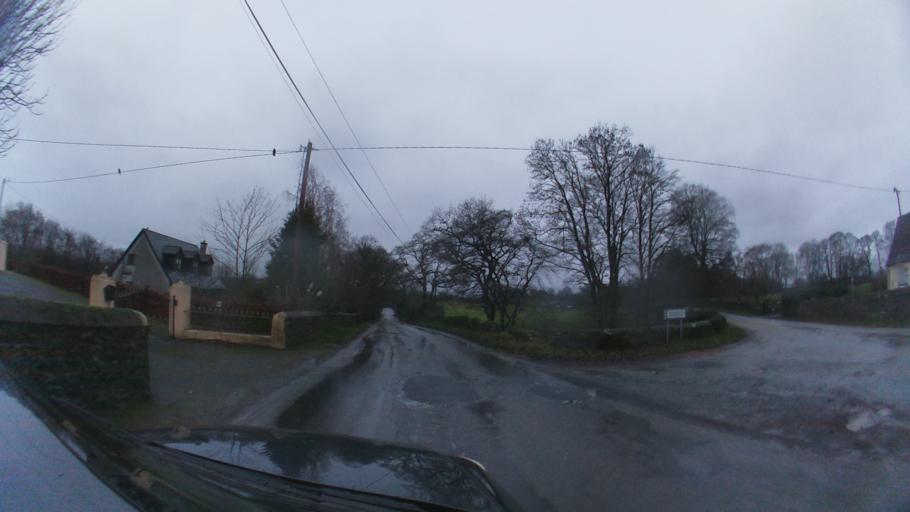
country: IE
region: Leinster
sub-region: County Carlow
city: Bagenalstown
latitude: 52.6577
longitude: -6.9908
